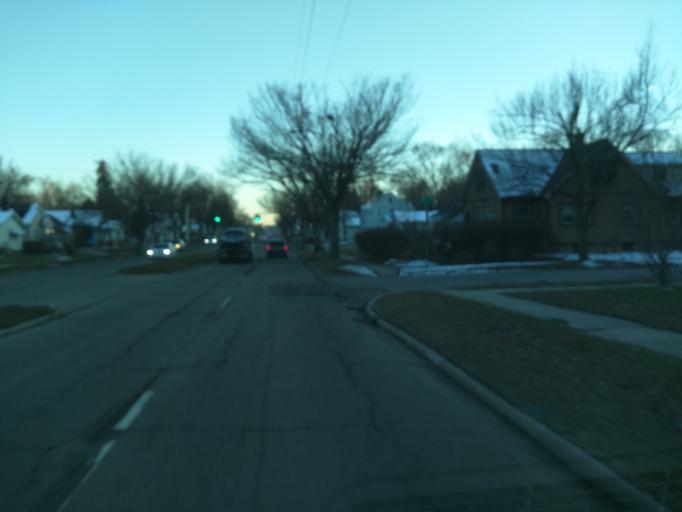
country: US
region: Michigan
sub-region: Ingham County
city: Lansing
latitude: 42.7094
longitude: -84.5382
